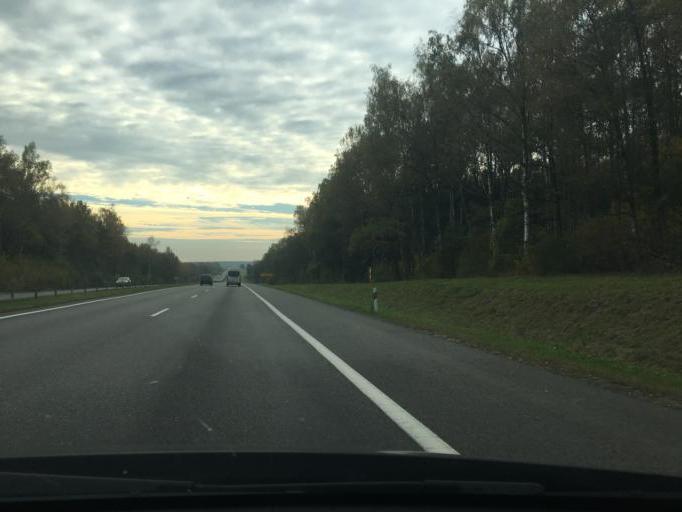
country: BY
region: Minsk
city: Enyerhyetykaw
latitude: 53.6346
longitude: 27.0624
